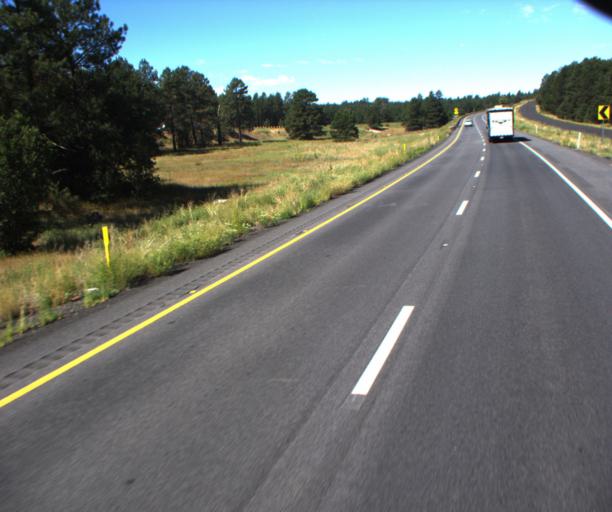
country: US
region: Arizona
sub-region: Coconino County
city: Williams
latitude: 35.2216
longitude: -112.2981
